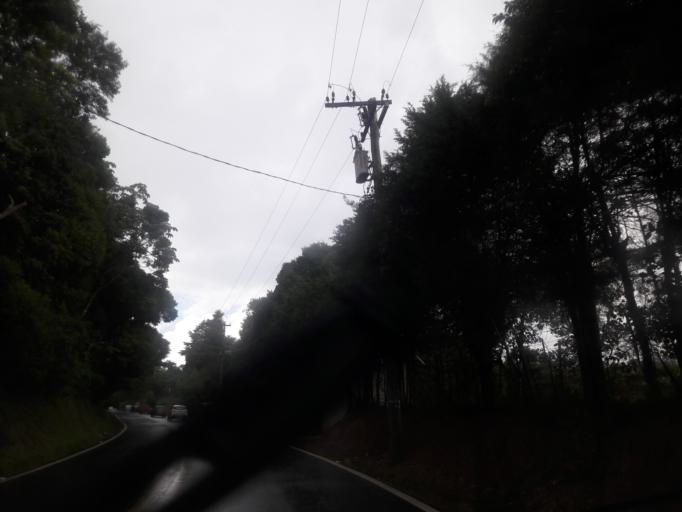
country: BR
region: Sao Paulo
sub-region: Aruja
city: Aruja
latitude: -23.3201
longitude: -46.4364
